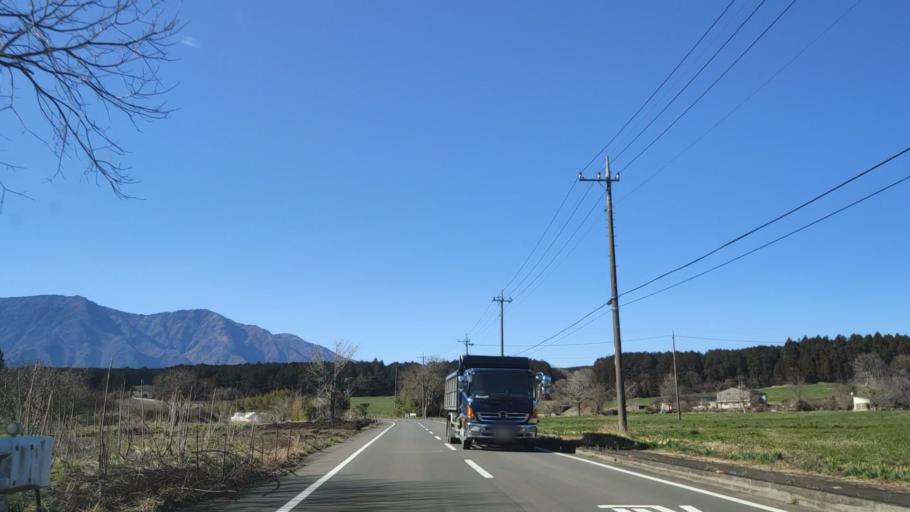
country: JP
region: Shizuoka
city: Fujinomiya
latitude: 35.3652
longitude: 138.6055
